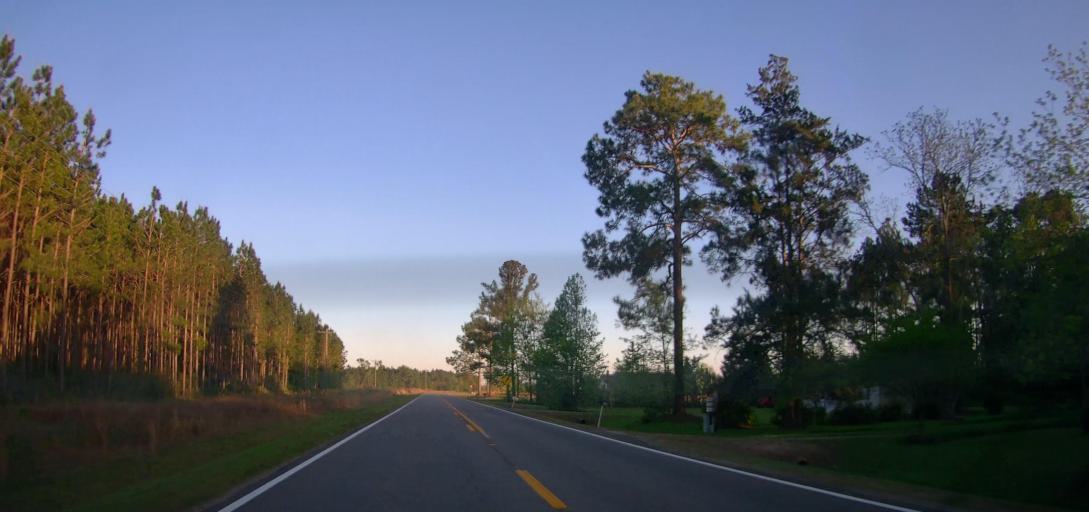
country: US
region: Georgia
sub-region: Irwin County
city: Ocilla
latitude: 31.6177
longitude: -83.2672
